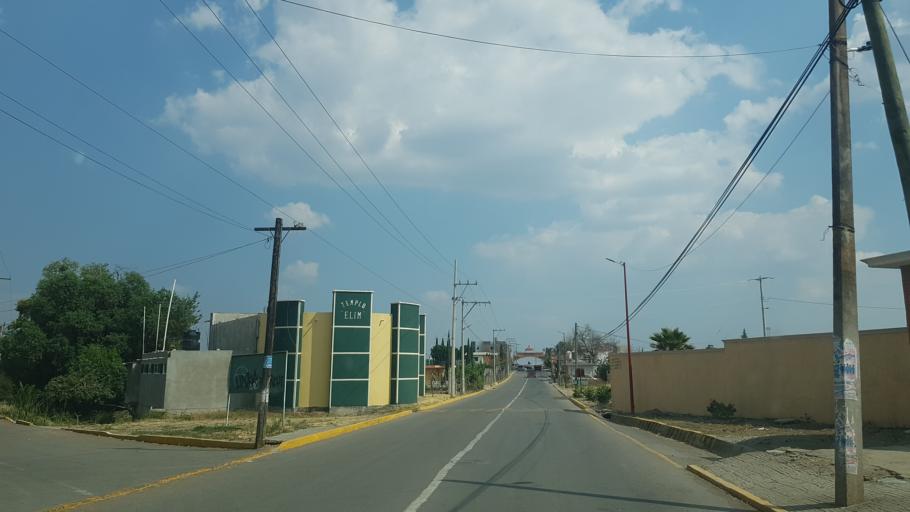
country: MX
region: Puebla
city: San Juan Amecac
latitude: 18.8295
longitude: -98.6576
